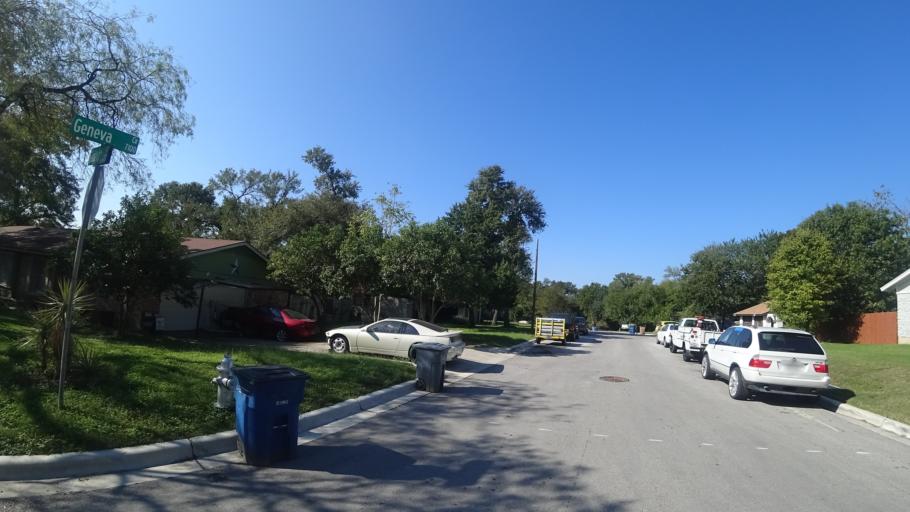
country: US
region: Texas
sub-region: Travis County
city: Austin
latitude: 30.3192
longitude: -97.6727
